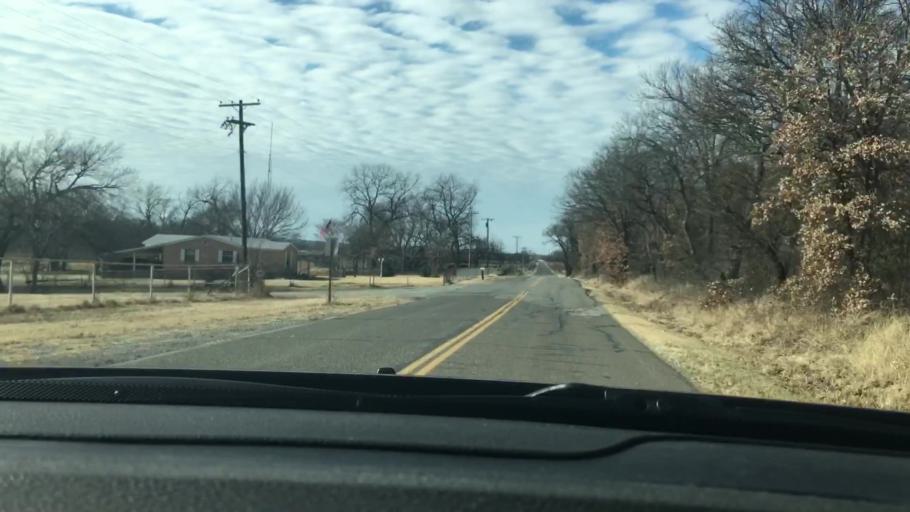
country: US
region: Oklahoma
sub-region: Garvin County
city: Pauls Valley
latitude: 34.7386
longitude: -97.1509
